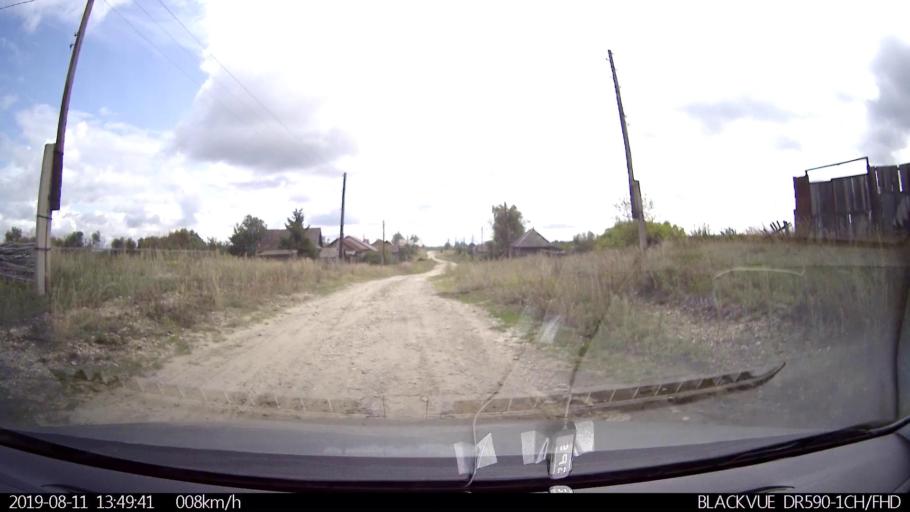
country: RU
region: Ulyanovsk
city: Ignatovka
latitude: 53.8474
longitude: 47.5807
